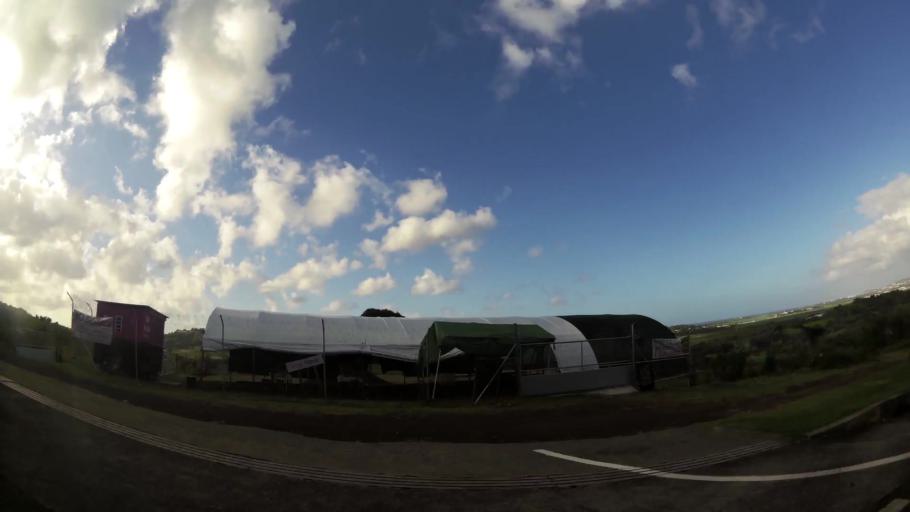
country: MQ
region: Martinique
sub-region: Martinique
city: Ducos
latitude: 14.6017
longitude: -60.9574
